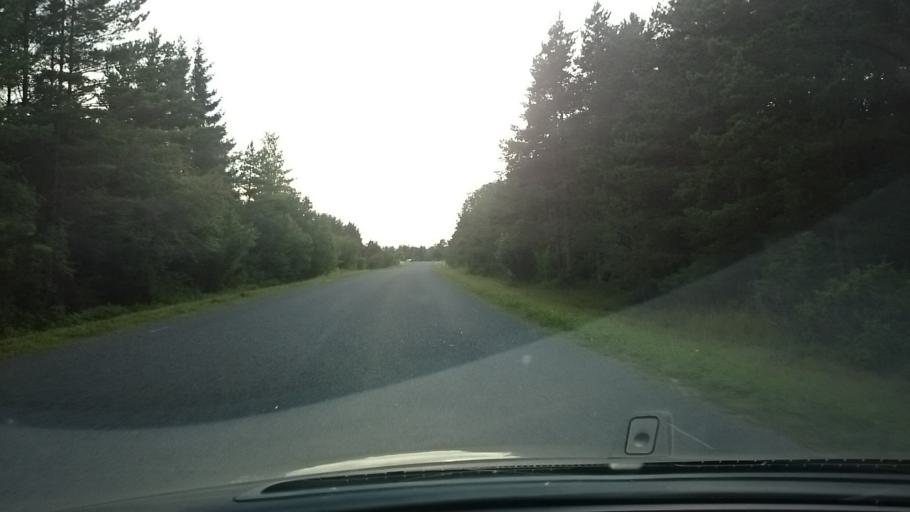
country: EE
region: Saare
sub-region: Kuressaare linn
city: Kuressaare
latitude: 58.4190
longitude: 22.1623
